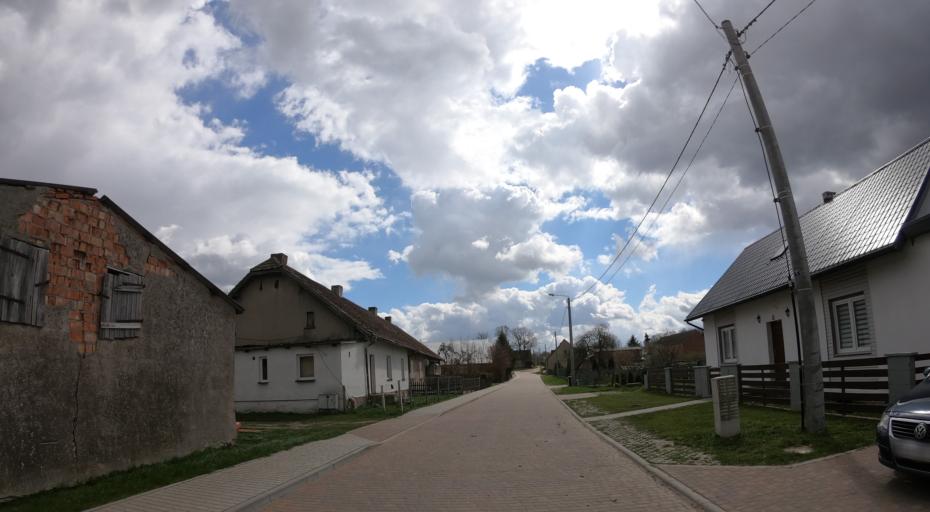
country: PL
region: West Pomeranian Voivodeship
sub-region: Powiat drawski
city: Drawsko Pomorskie
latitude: 53.5411
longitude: 15.8694
